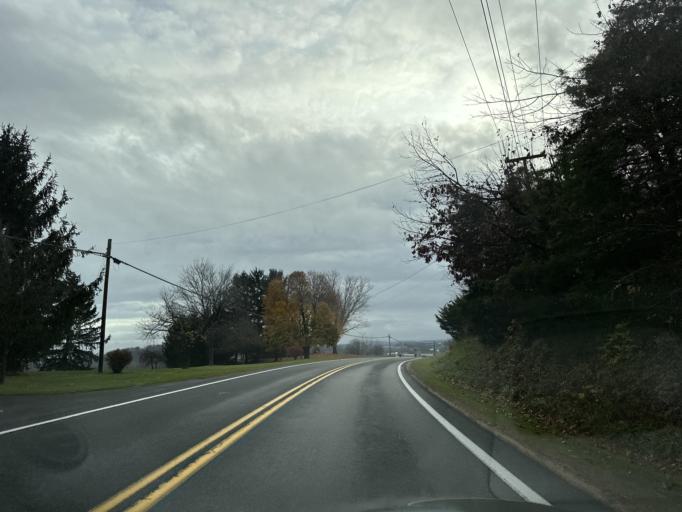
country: US
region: Virginia
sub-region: Rockingham County
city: Bridgewater
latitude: 38.4177
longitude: -78.9990
